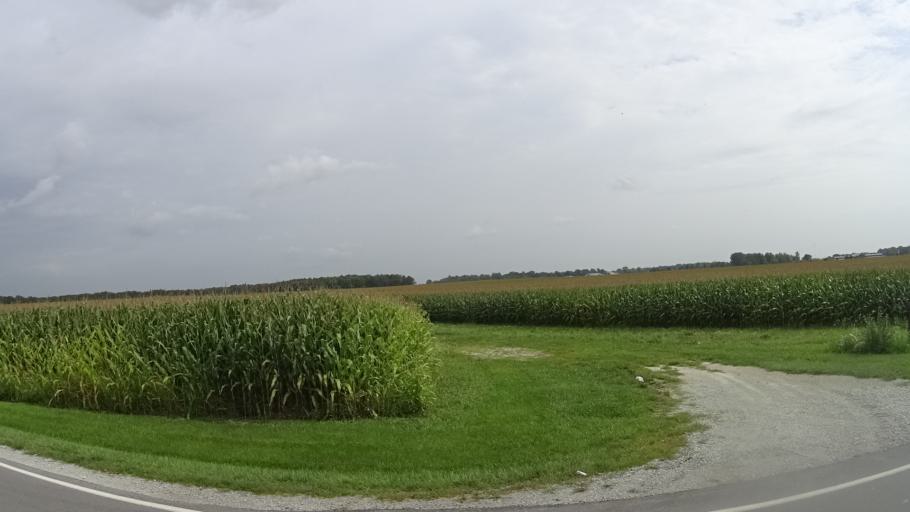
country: US
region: Indiana
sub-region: Madison County
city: Pendleton
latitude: 40.0066
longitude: -85.7827
